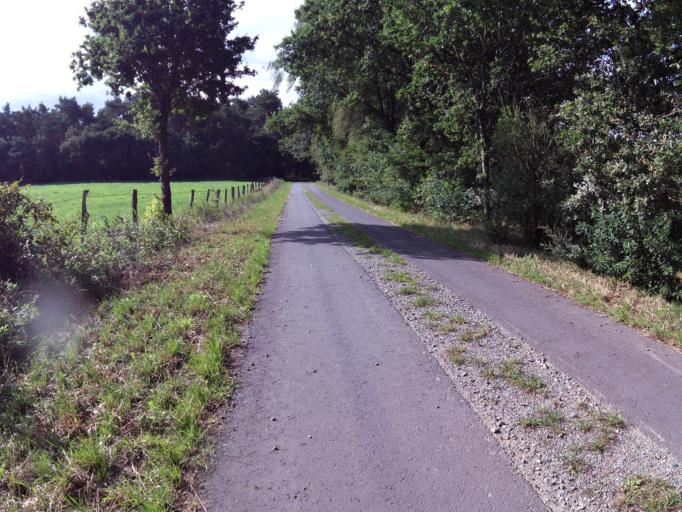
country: DE
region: Lower Saxony
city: Bremervorde
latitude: 53.4494
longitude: 9.1257
